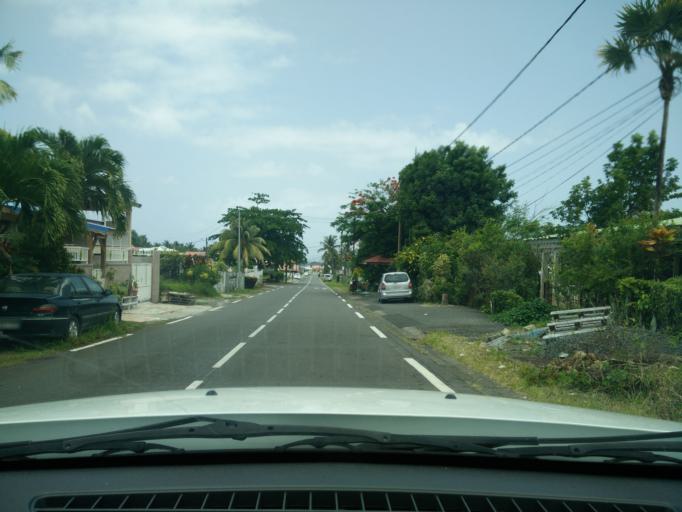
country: GP
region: Guadeloupe
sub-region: Guadeloupe
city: Capesterre-Belle-Eau
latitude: 16.0533
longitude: -61.5609
